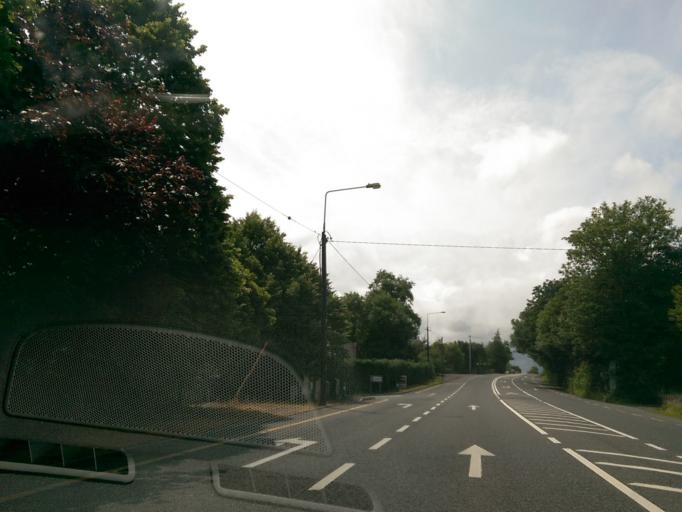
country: IE
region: Munster
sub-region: An Clar
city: Ennis
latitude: 52.8254
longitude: -9.0044
